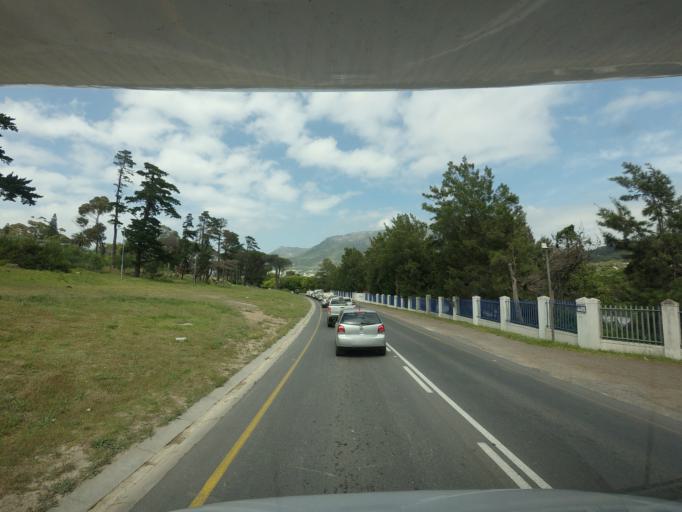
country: ZA
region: Western Cape
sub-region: City of Cape Town
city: Constantia
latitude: -34.0260
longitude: 18.3590
